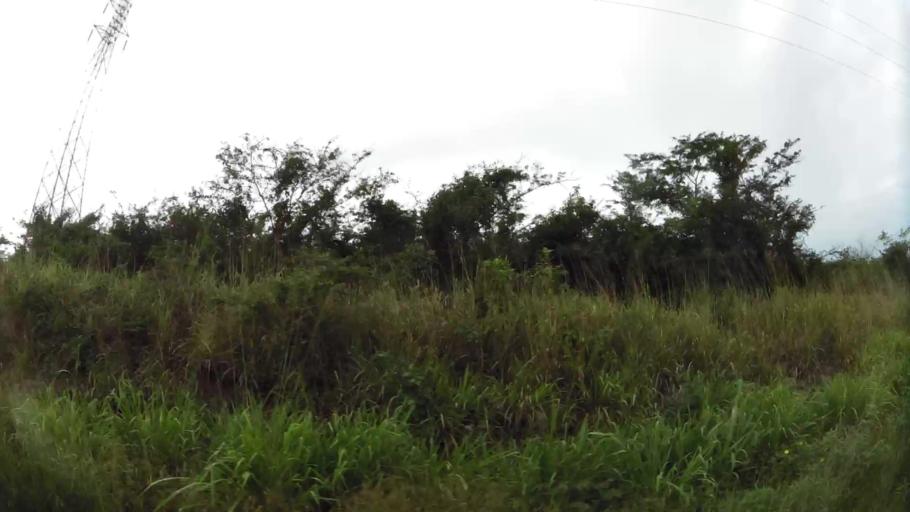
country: AG
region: Saint John
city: Potters Village
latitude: 17.1017
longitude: -61.8124
